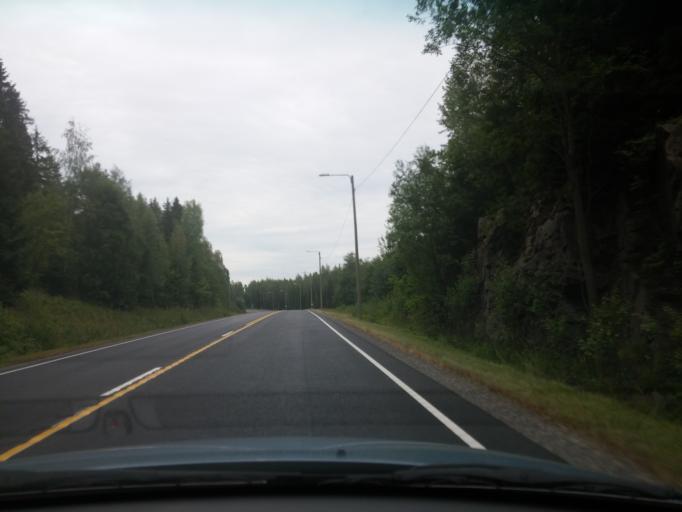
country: FI
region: Haeme
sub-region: Riihimaeki
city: Loppi
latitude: 60.7170
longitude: 24.4652
